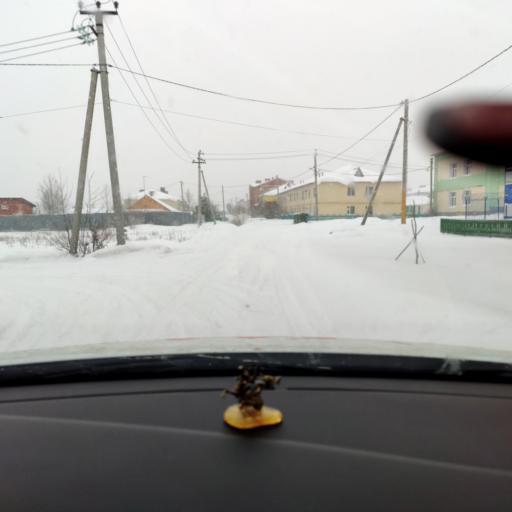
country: RU
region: Tatarstan
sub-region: Arskiy Rayon
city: Arsk
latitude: 56.0987
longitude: 49.8773
